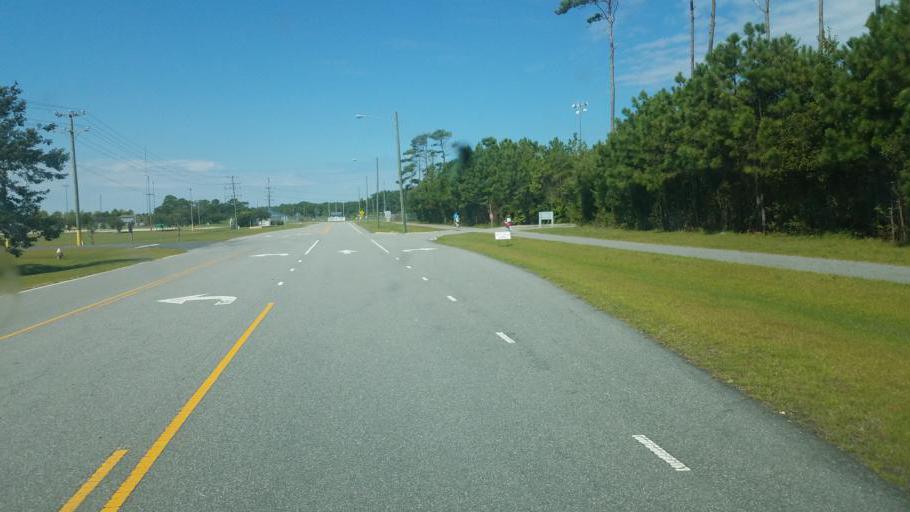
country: US
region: North Carolina
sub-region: Dare County
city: Kill Devil Hills
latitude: 36.0075
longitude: -75.6661
